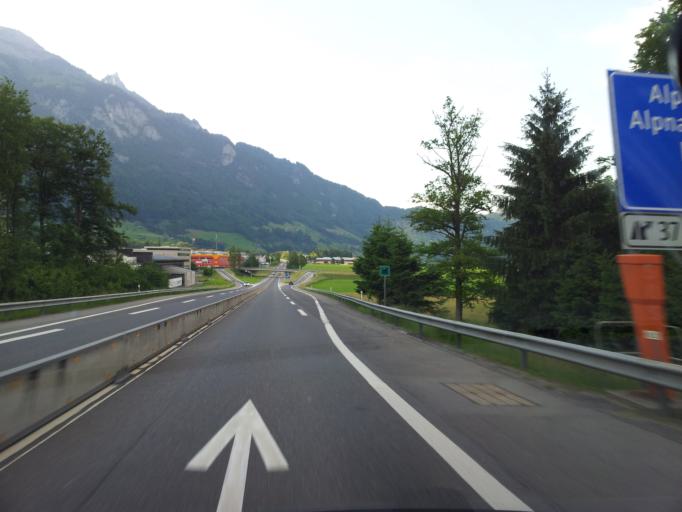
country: CH
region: Obwalden
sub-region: Obwalden
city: Alpnach
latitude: 46.9313
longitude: 8.2771
